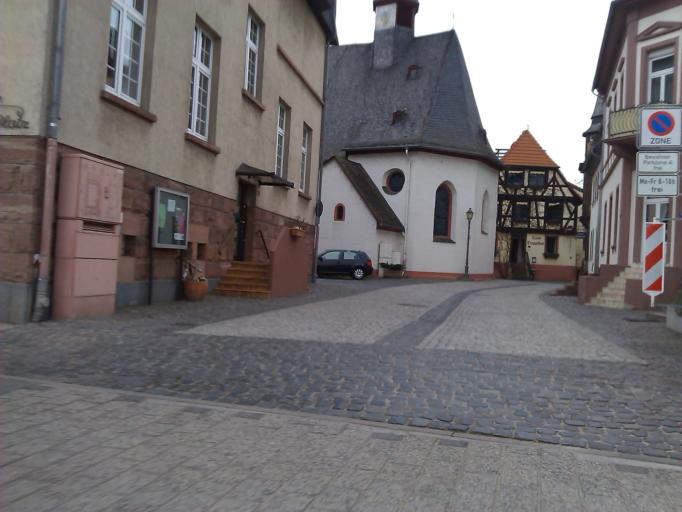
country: DE
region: Rheinland-Pfalz
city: Budenheim
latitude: 50.0342
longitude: 8.1615
